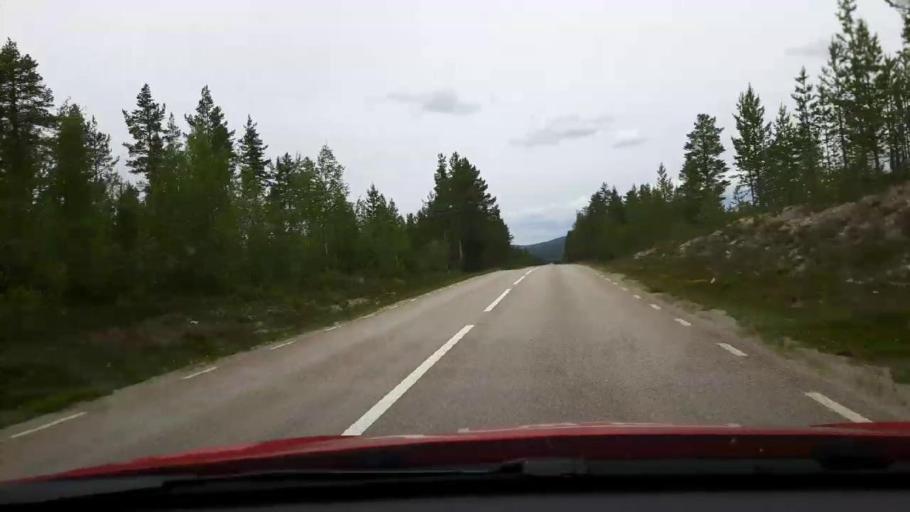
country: SE
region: Jaemtland
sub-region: Harjedalens Kommun
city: Sveg
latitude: 62.2505
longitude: 13.8420
